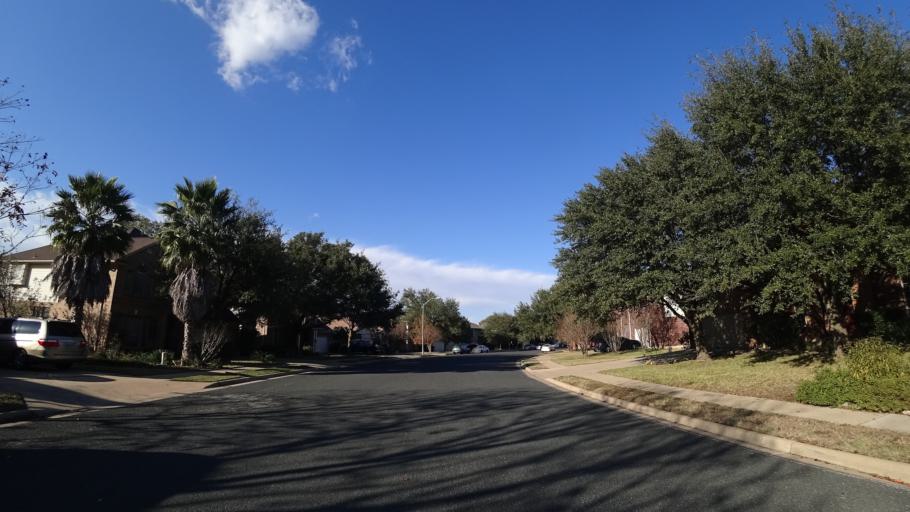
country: US
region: Texas
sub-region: Williamson County
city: Brushy Creek
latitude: 30.4982
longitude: -97.7481
